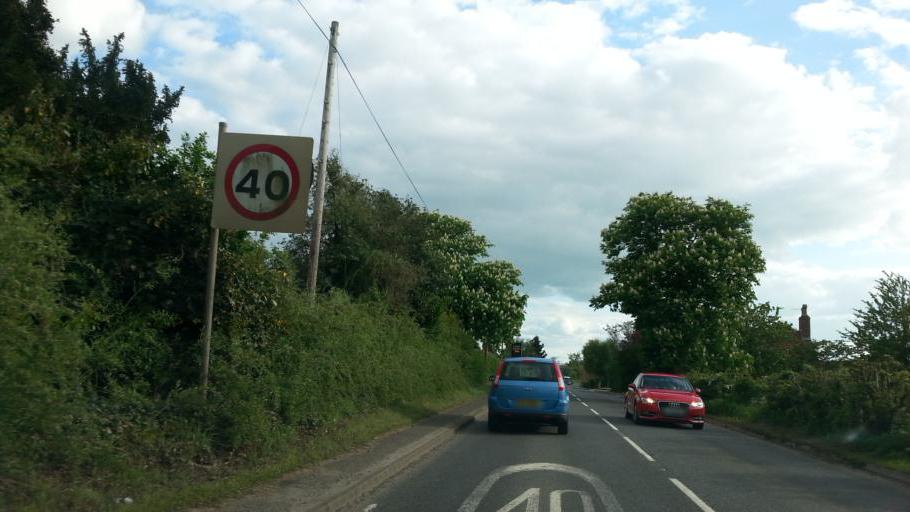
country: GB
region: England
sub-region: Nottinghamshire
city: South Collingham
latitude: 53.1175
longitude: -0.7720
